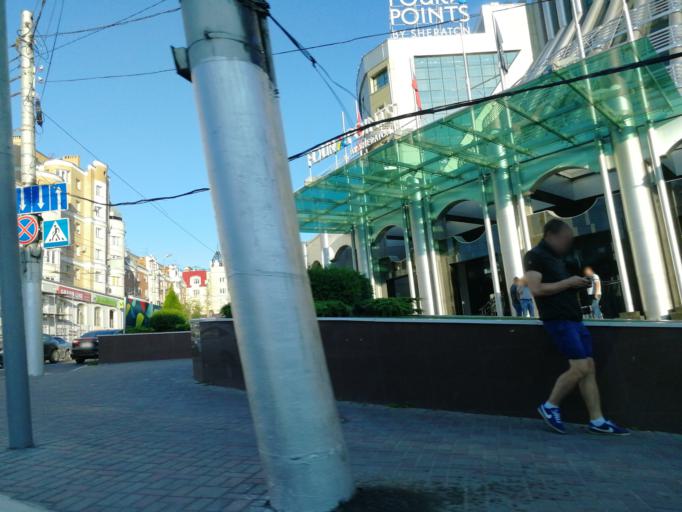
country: RU
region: Kaluga
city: Kaluga
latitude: 54.5134
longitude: 36.2389
